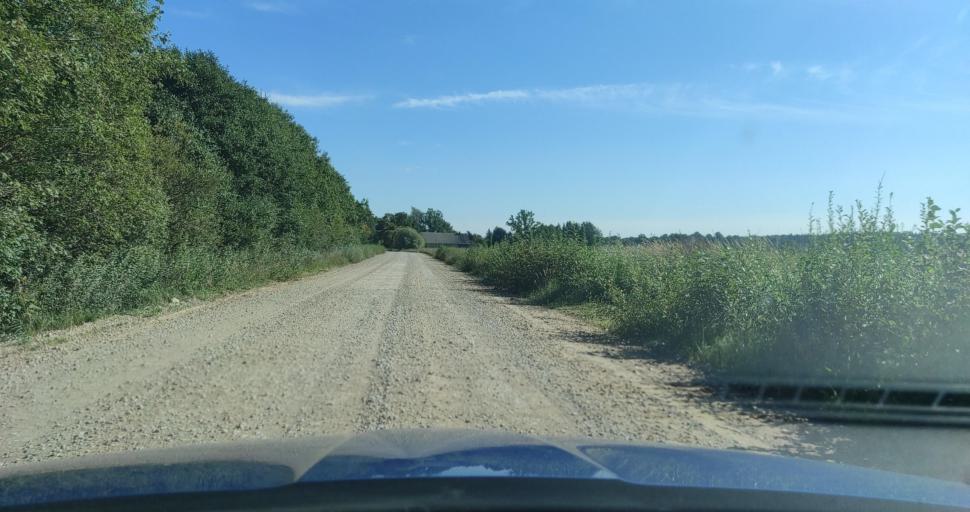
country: LV
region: Aizpute
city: Aizpute
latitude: 56.8140
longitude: 21.4653
